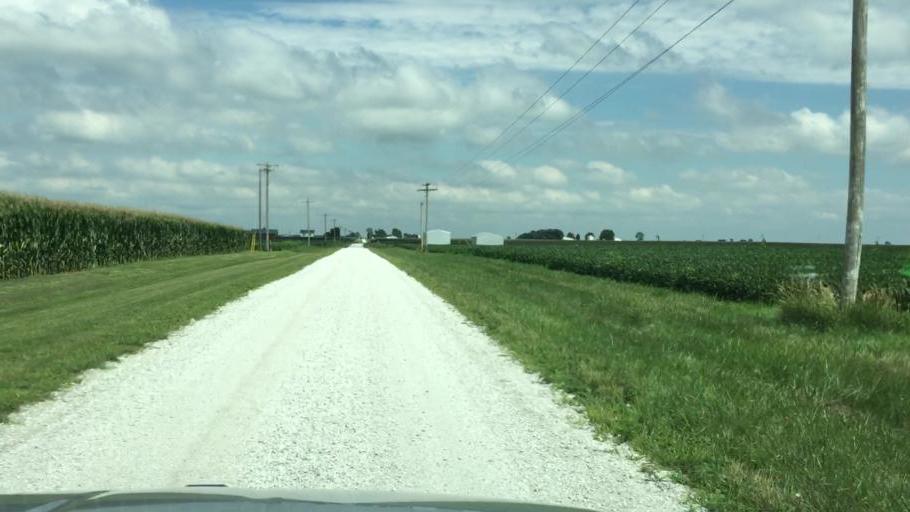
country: US
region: Illinois
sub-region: Hancock County
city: Nauvoo
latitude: 40.5215
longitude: -91.2848
